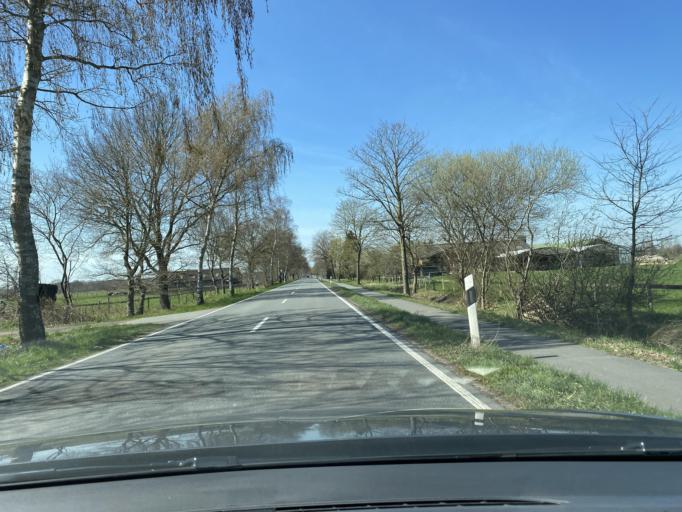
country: DE
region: Lower Saxony
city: Wilstedt
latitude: 53.1259
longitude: 9.0502
